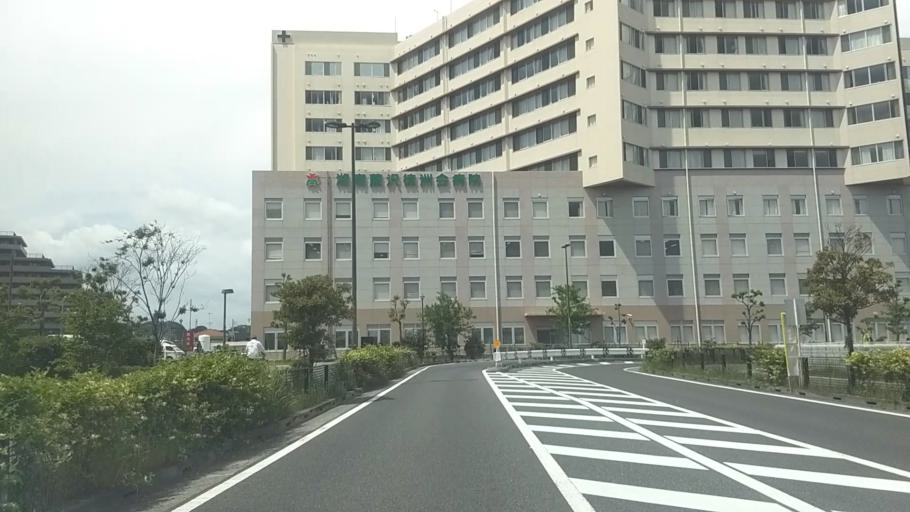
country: JP
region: Kanagawa
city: Fujisawa
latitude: 35.3400
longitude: 139.4446
